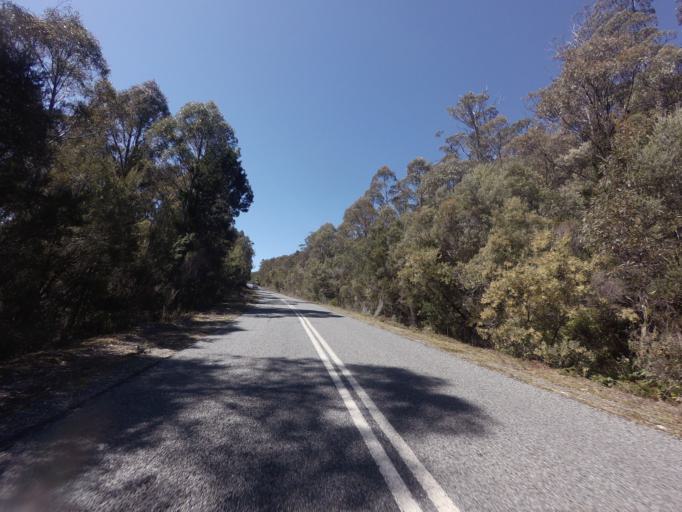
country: AU
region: Tasmania
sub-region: Huon Valley
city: Geeveston
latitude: -42.8121
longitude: 146.3898
